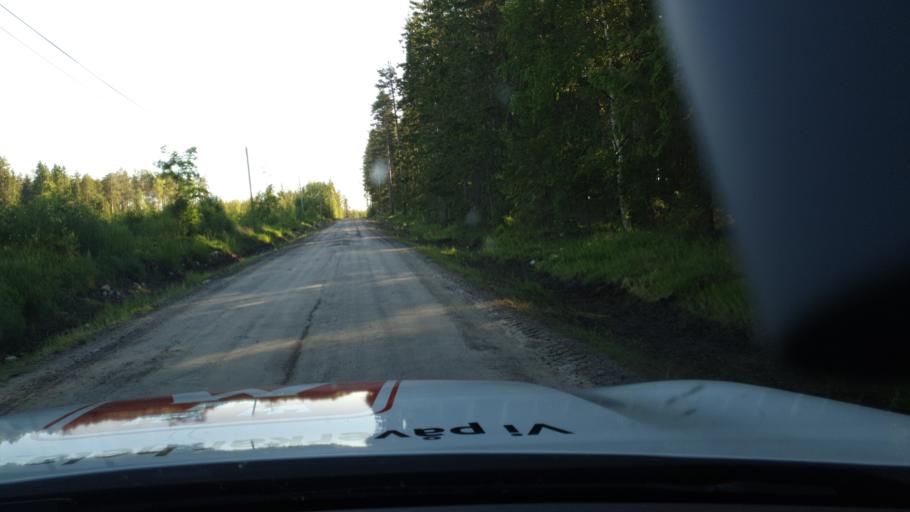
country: SE
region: Vaesterbotten
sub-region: Umea Kommun
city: Roback
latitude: 64.0082
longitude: 20.0716
